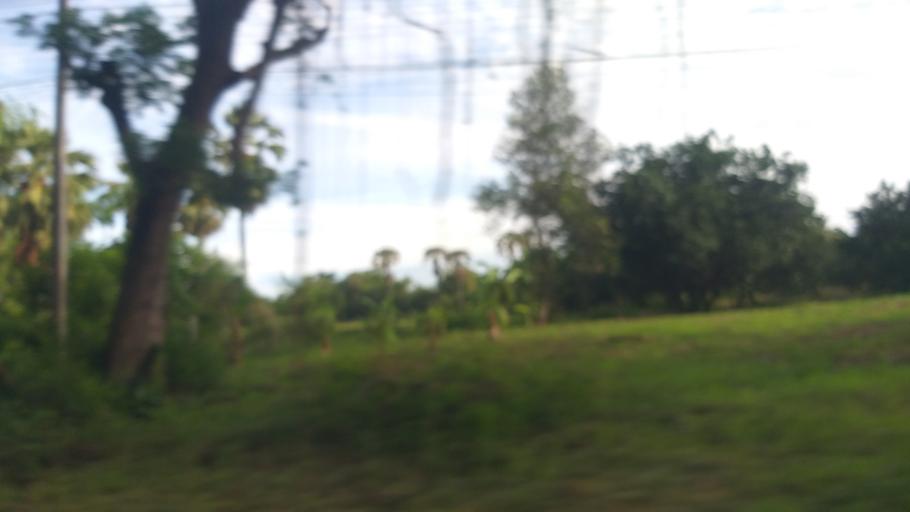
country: TH
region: Chaiyaphum
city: Ban Thaen
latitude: 16.3856
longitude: 102.3176
